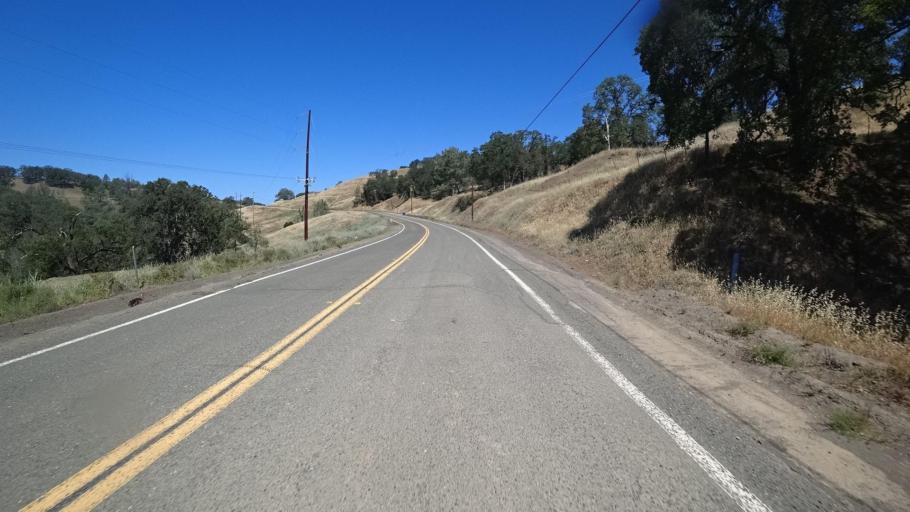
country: US
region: California
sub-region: Lake County
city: Lower Lake
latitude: 38.8933
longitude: -122.5451
